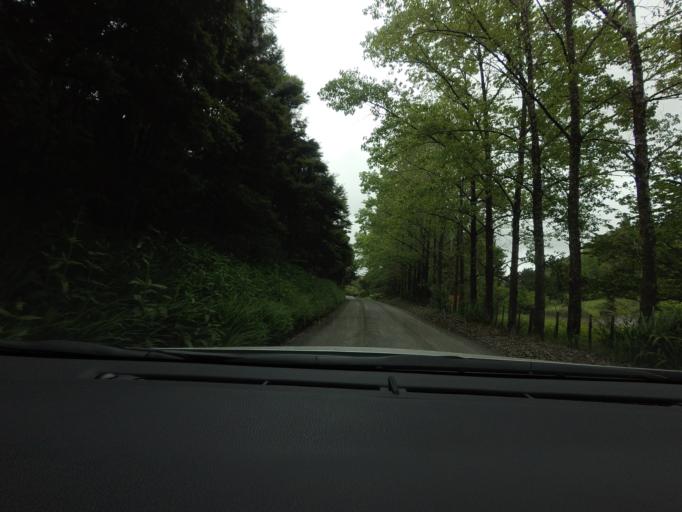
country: NZ
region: Auckland
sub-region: Auckland
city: Warkworth
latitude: -36.4774
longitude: 174.5636
